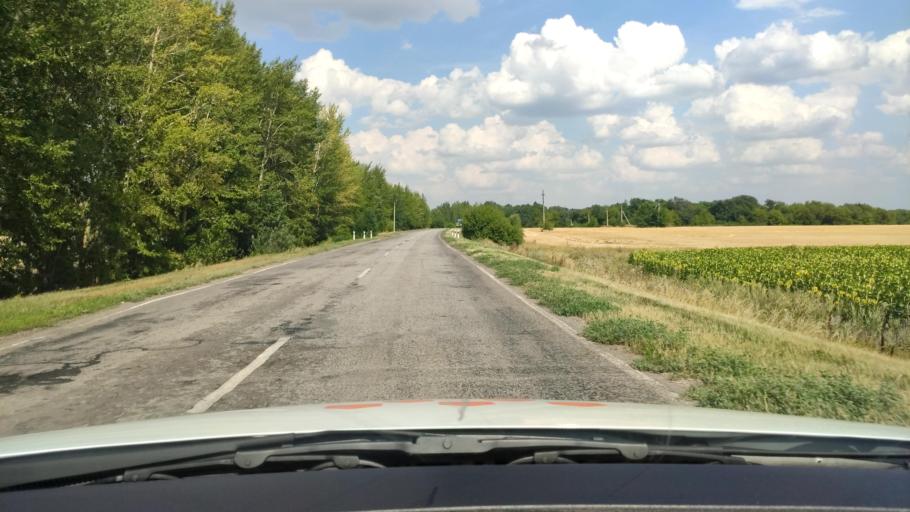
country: RU
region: Voronezj
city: Pereleshinskiy
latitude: 51.7546
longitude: 40.4228
